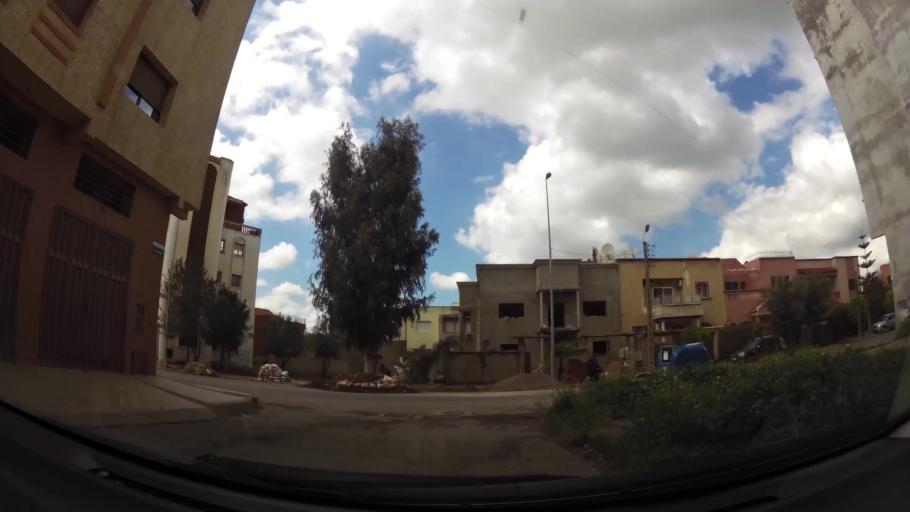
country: MA
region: Chaouia-Ouardigha
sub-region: Settat Province
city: Berrechid
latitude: 33.2756
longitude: -7.5912
